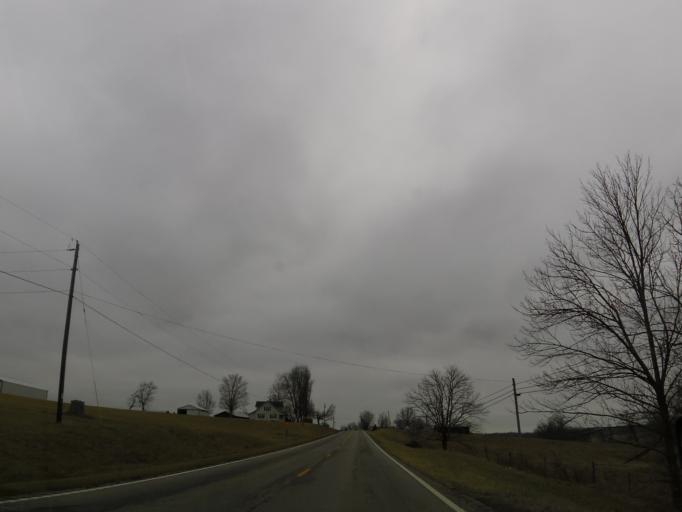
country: US
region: Kentucky
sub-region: Trimble County
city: Providence
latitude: 38.5178
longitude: -85.1881
